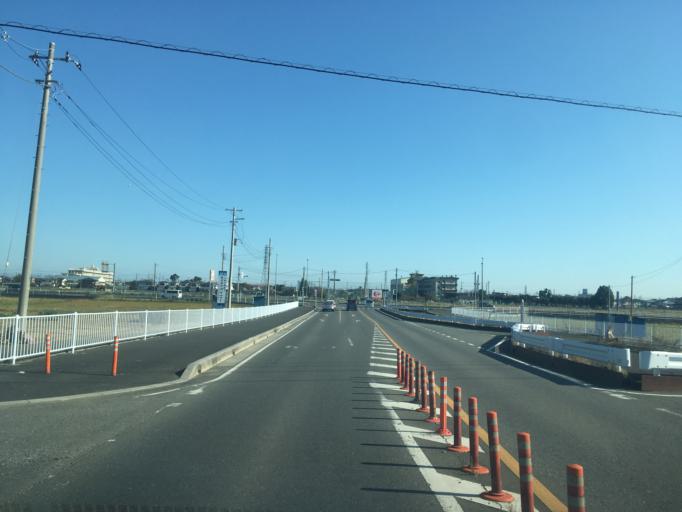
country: JP
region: Saitama
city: Kawagoe
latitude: 35.9408
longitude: 139.4703
